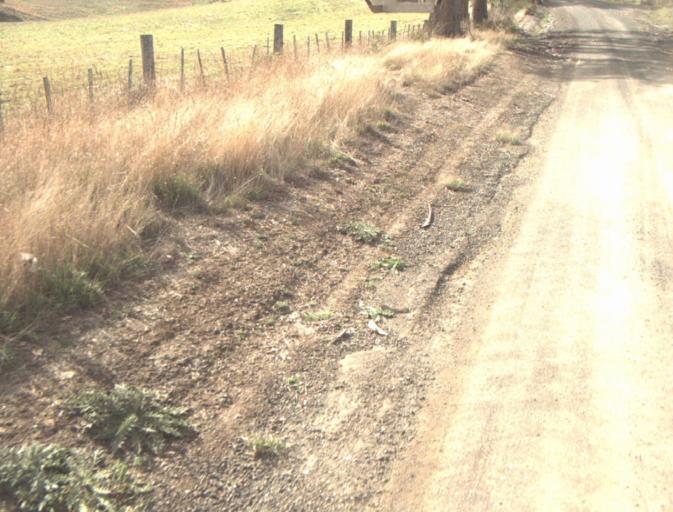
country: AU
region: Tasmania
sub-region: Launceston
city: Mayfield
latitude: -41.1858
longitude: 147.1922
